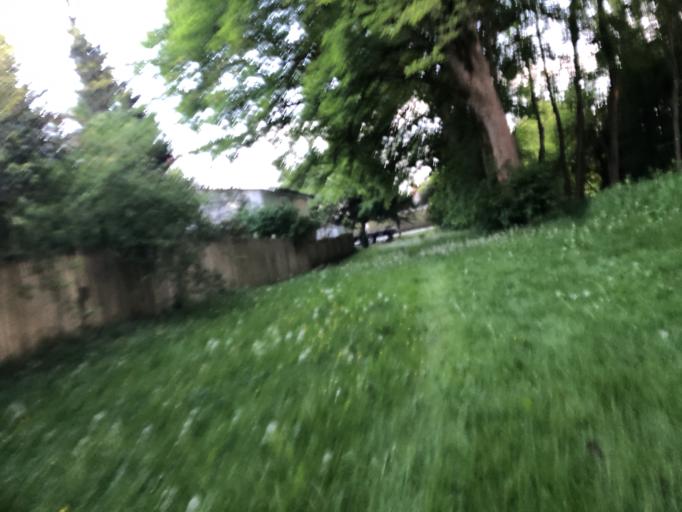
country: CA
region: British Columbia
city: Richmond
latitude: 49.1342
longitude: -123.1253
